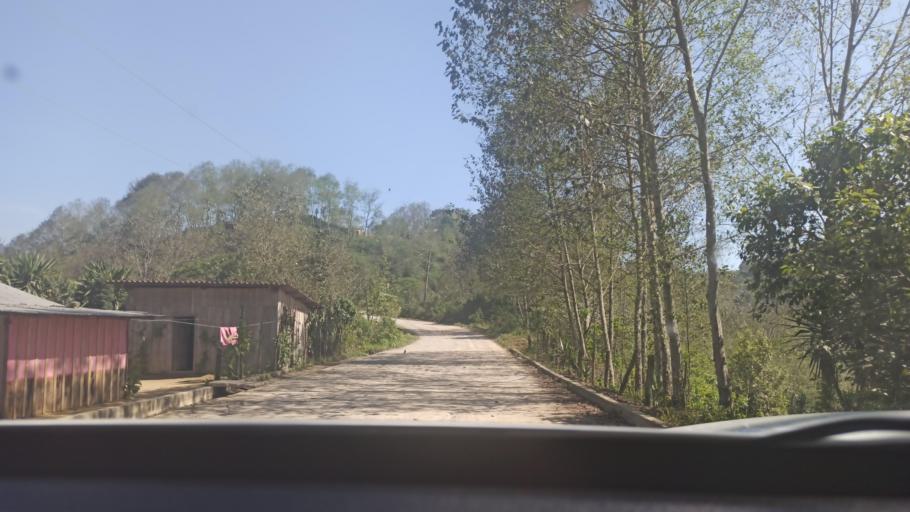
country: MX
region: Veracruz
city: Xocotla
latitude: 18.9723
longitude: -97.0907
